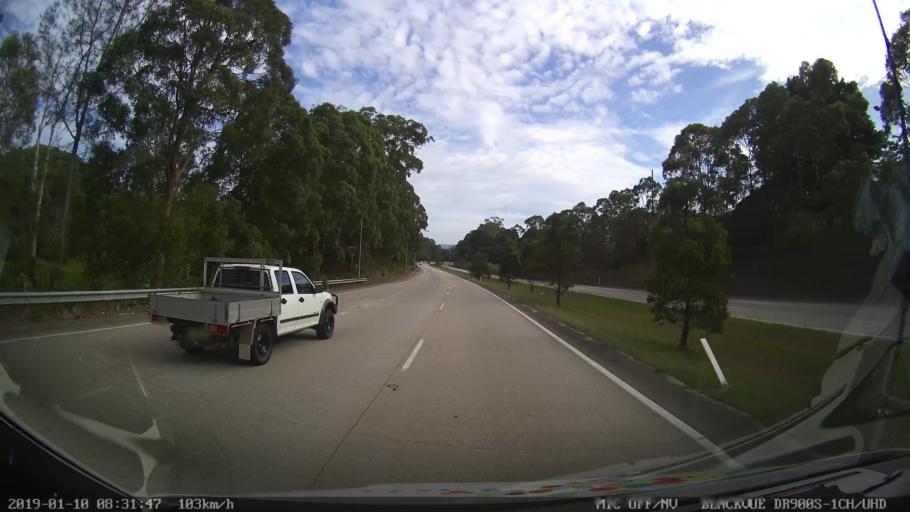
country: AU
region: New South Wales
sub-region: Coffs Harbour
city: Boambee
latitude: -30.3519
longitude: 153.0645
